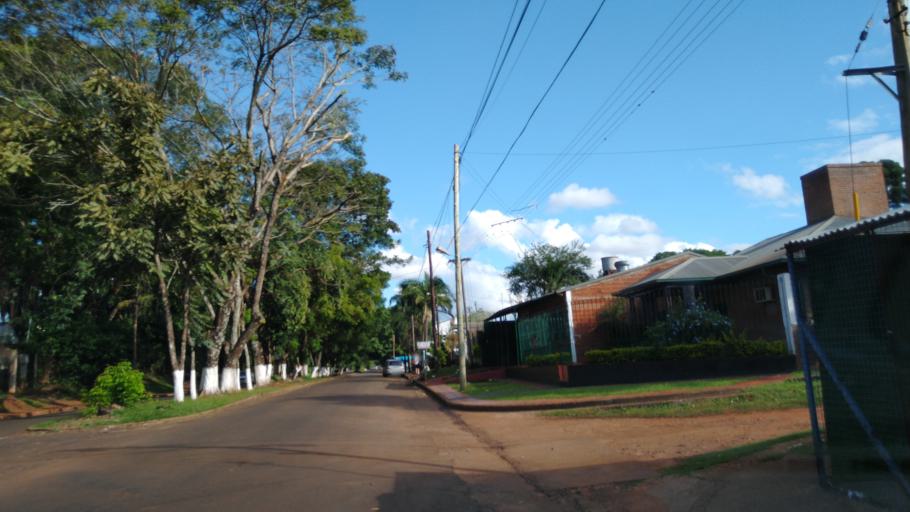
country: AR
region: Misiones
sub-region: Departamento de Capital
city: Posadas
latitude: -27.3670
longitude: -55.9241
